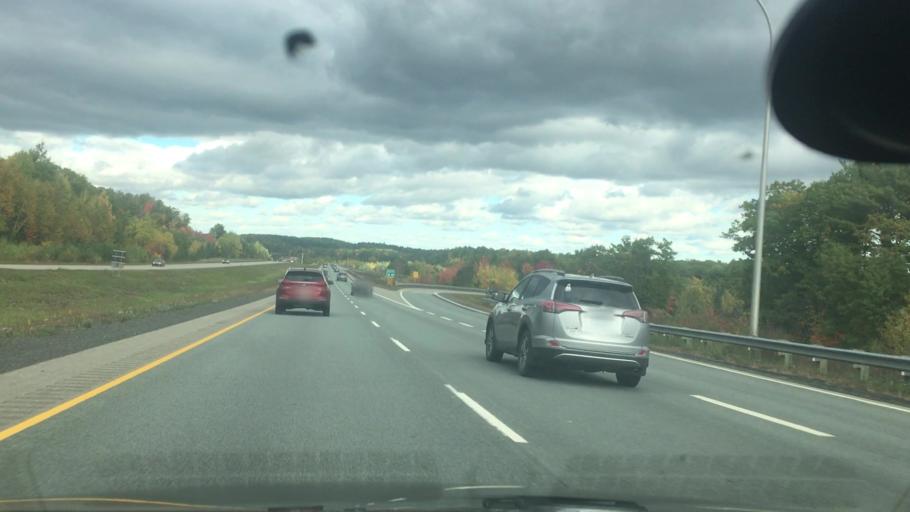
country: CA
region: Nova Scotia
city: Windsor
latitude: 44.9560
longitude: -64.0115
